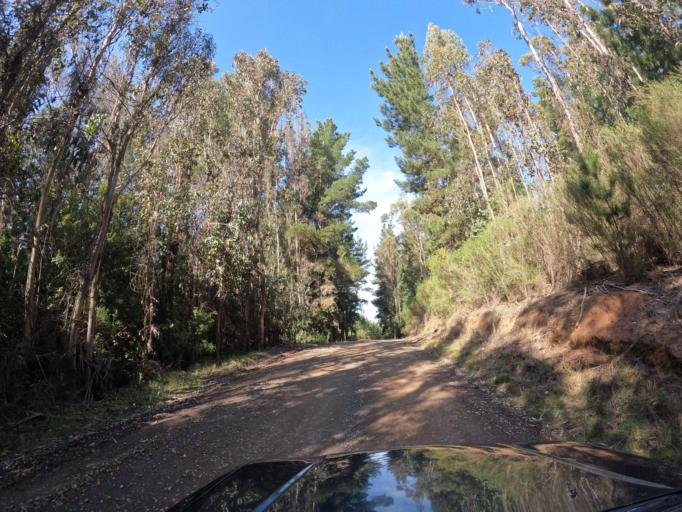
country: CL
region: Biobio
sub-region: Provincia de Biobio
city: La Laja
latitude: -37.0830
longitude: -72.7857
